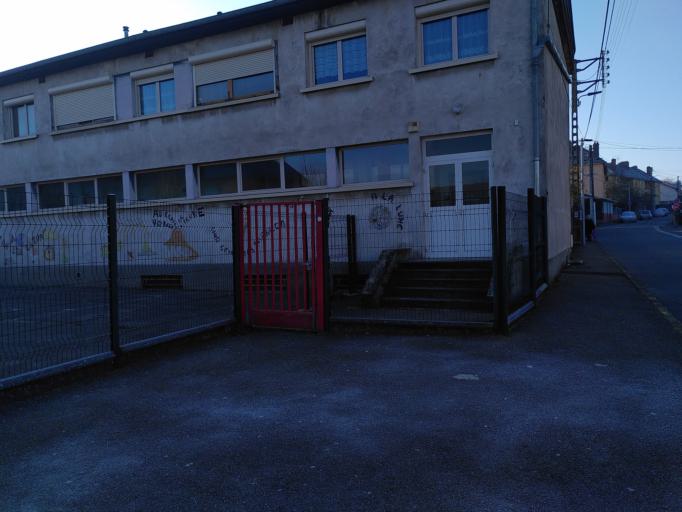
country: FR
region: Lorraine
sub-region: Departement de Meurthe-et-Moselle
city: Dieulouard
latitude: 48.8379
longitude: 6.0691
